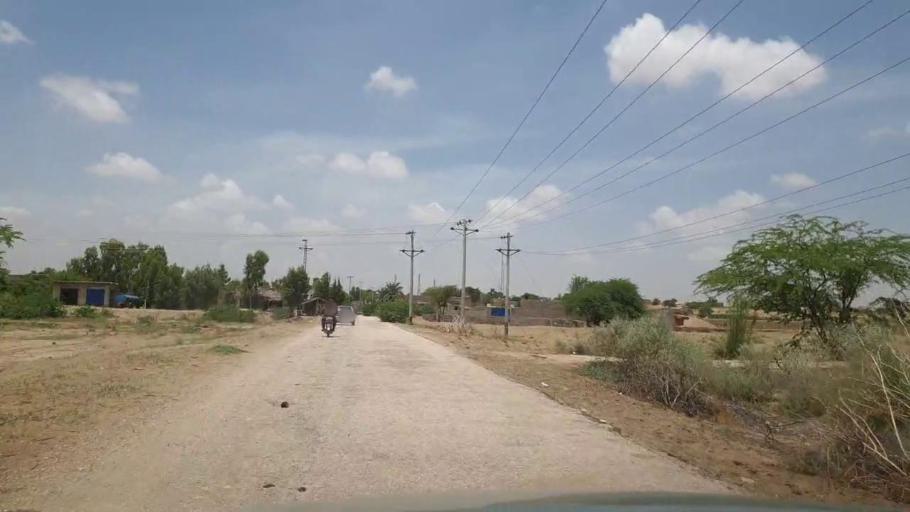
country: PK
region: Sindh
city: Kot Diji
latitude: 27.1587
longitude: 68.9682
